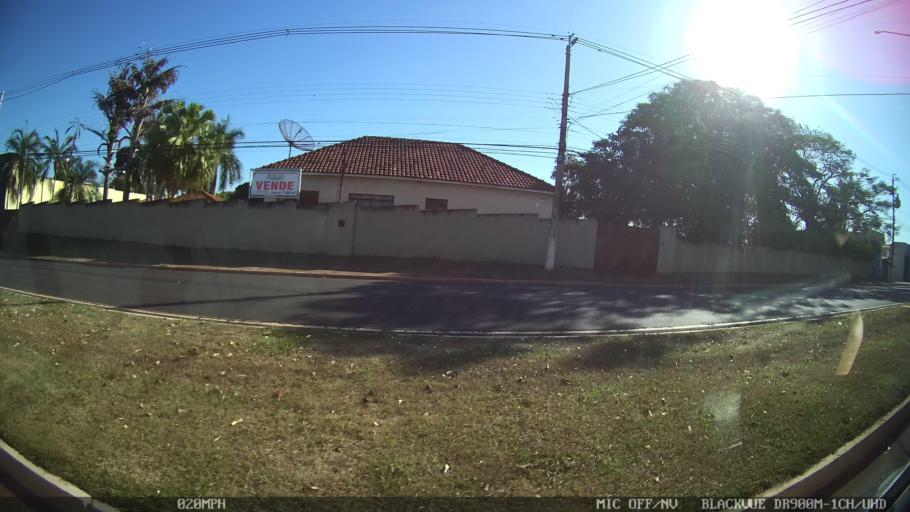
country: BR
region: Sao Paulo
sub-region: Olimpia
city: Olimpia
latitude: -20.7314
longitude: -48.9050
